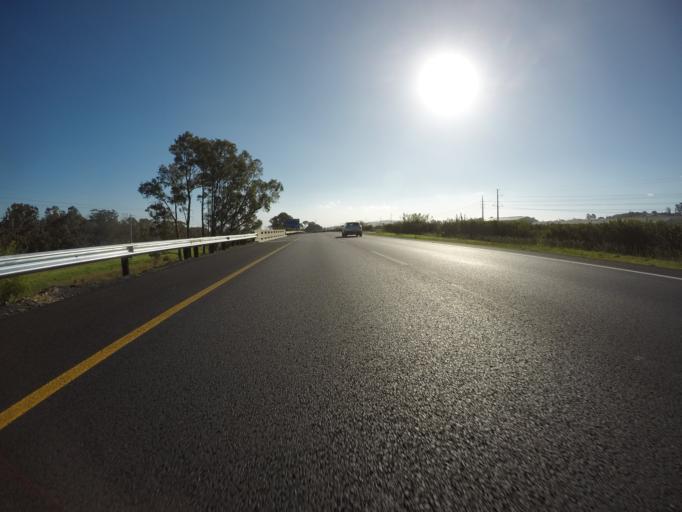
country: ZA
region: Western Cape
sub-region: Cape Winelands District Municipality
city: Stellenbosch
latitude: -34.0606
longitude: 18.7970
